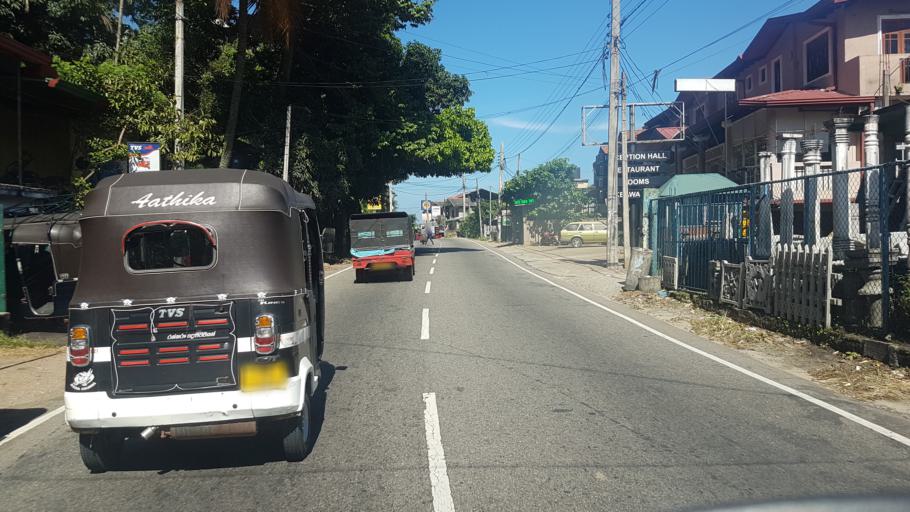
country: LK
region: Central
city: Kandy
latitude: 7.2886
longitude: 80.6572
